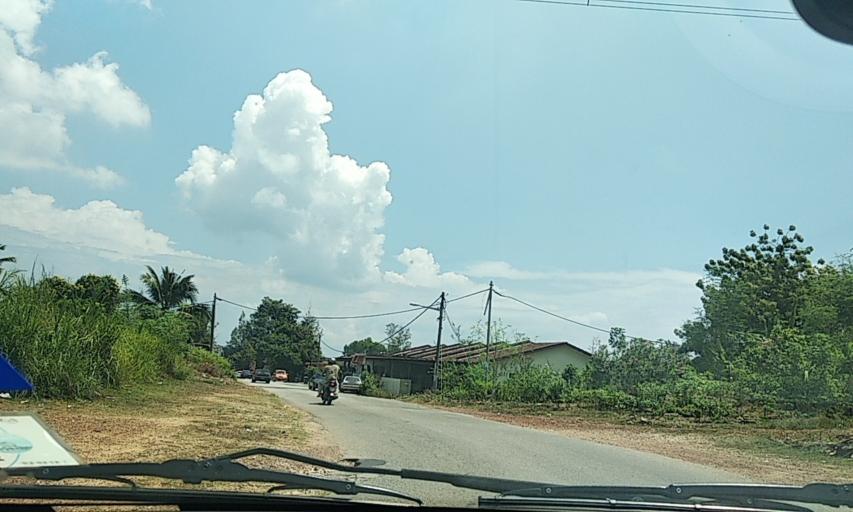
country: MY
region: Kedah
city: Sungai Petani
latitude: 5.6246
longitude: 100.4722
